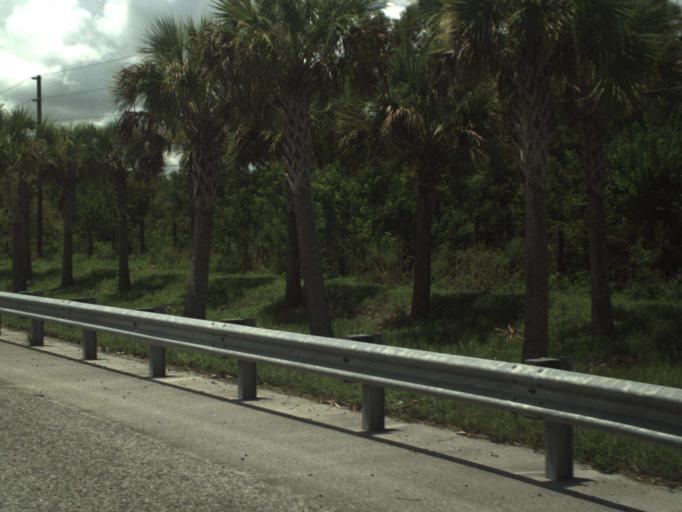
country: US
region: Florida
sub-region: Indian River County
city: Fellsmere
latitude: 27.6667
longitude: -80.8000
